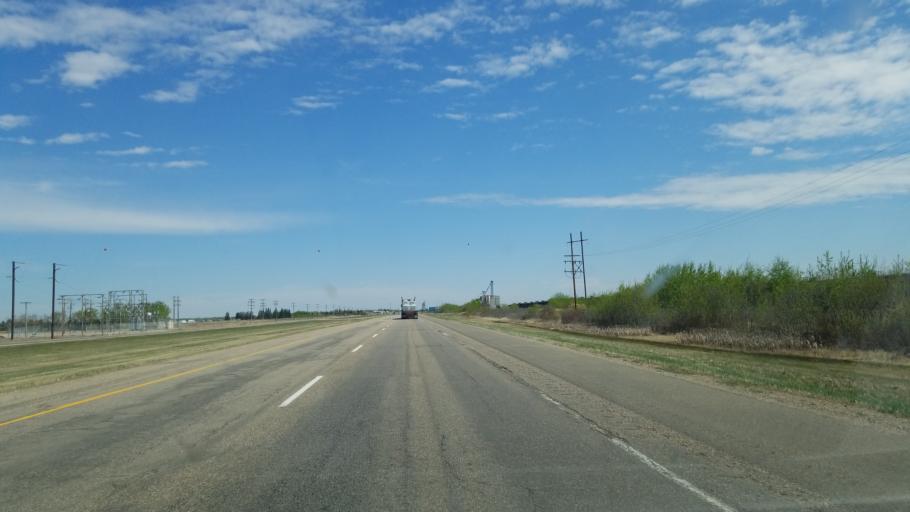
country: CA
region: Saskatchewan
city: Lloydminster
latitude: 53.1394
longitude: -109.6539
